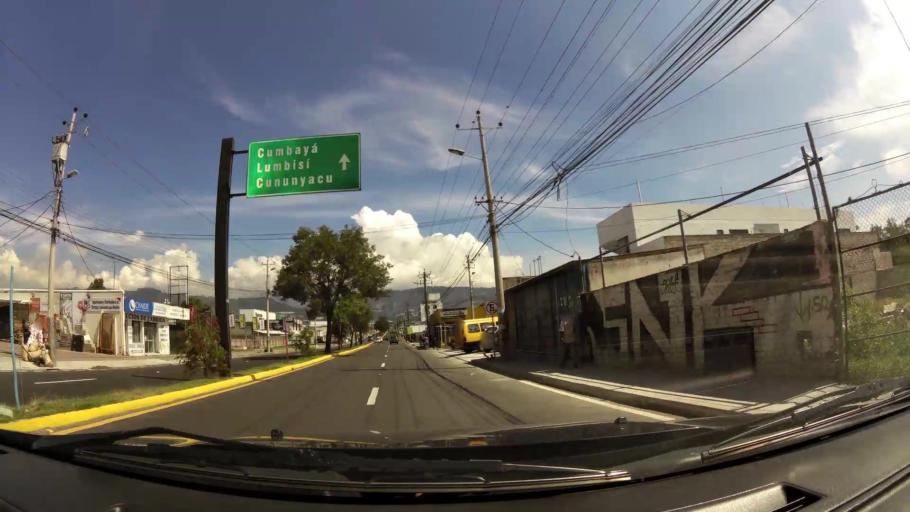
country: EC
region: Pichincha
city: Quito
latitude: -0.2134
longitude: -78.4092
